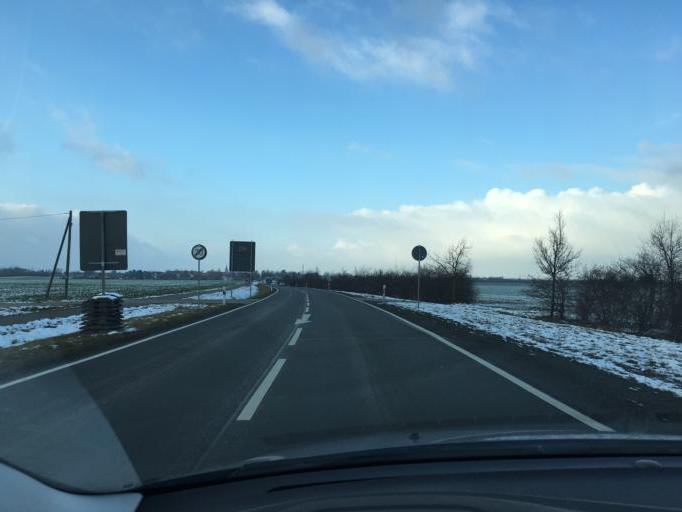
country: DE
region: Saxony
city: Brandis
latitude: 51.3453
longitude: 12.5966
